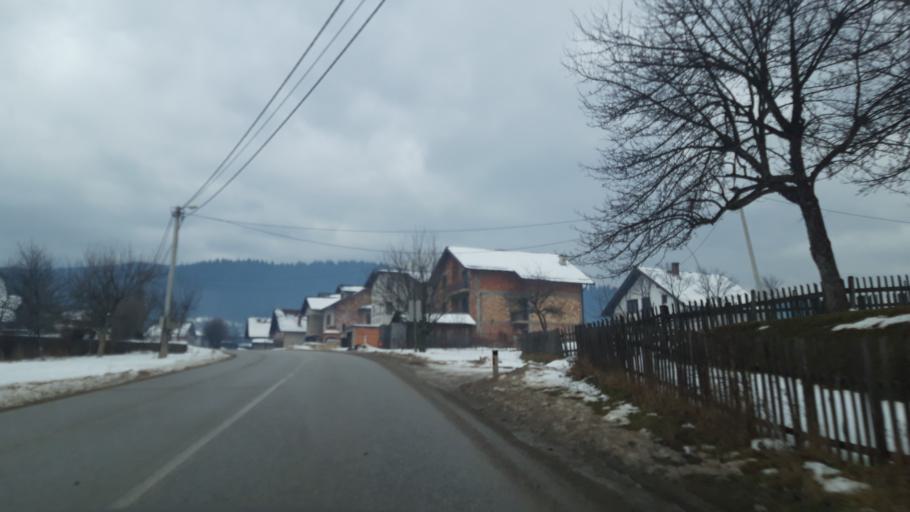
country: BA
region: Republika Srpska
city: Koran
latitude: 43.8097
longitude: 18.5571
